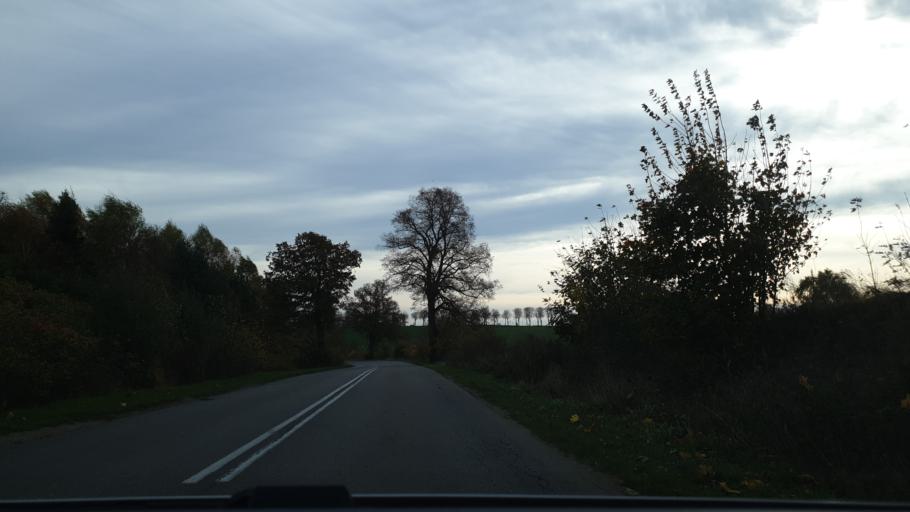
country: PL
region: Pomeranian Voivodeship
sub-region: Powiat pucki
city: Gniezdzewo
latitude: 54.7120
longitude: 18.3416
